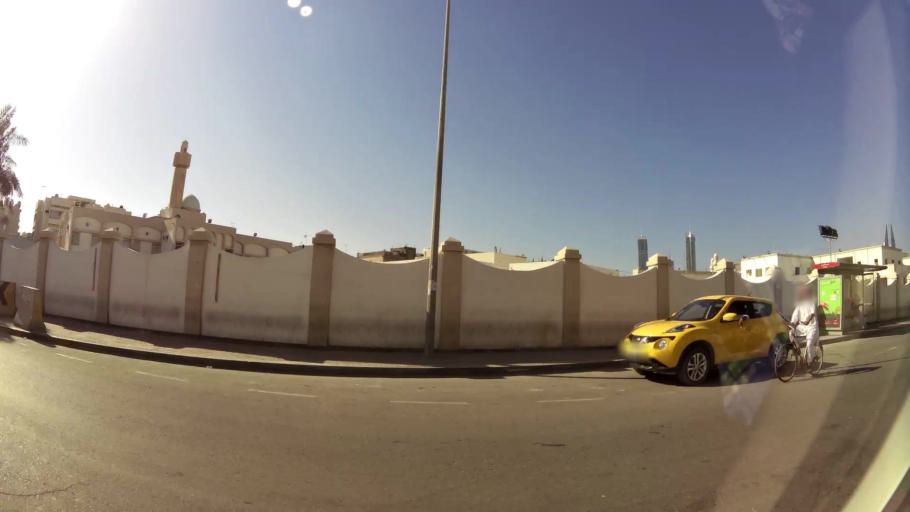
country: BH
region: Manama
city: Manama
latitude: 26.2258
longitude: 50.5779
